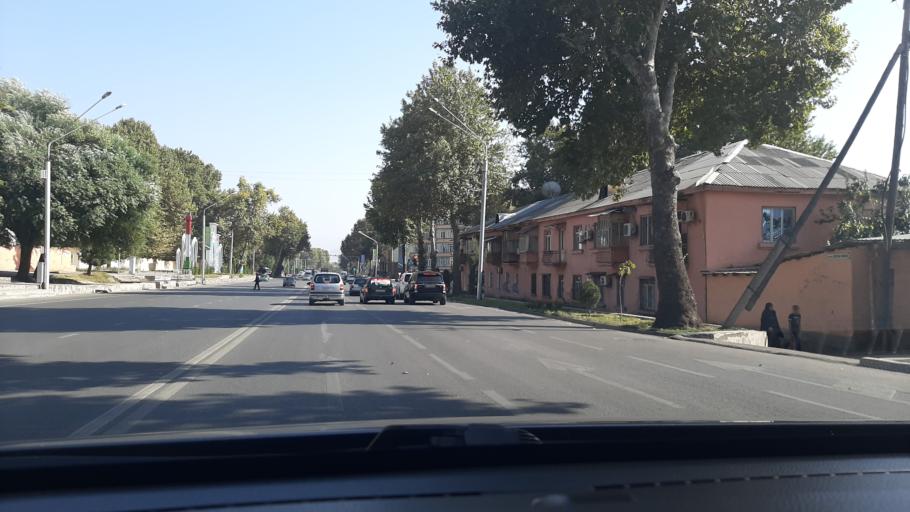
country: TJ
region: Dushanbe
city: Dushanbe
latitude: 38.5686
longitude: 68.8125
